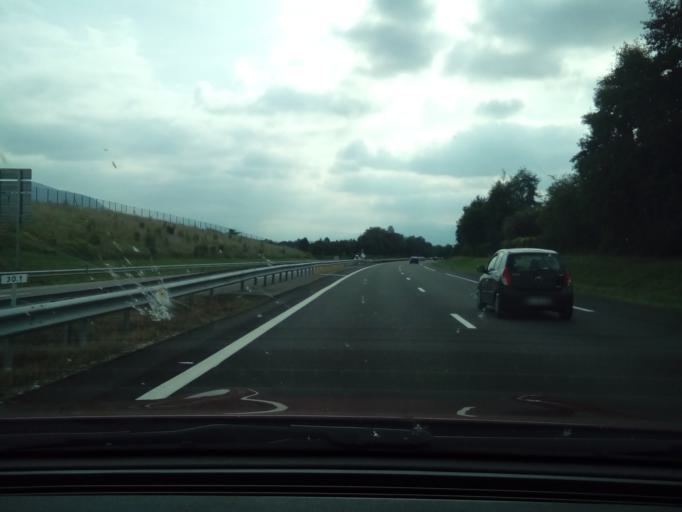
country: FR
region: Rhone-Alpes
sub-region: Departement de l'Isere
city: Saint-Sauveur
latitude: 45.1544
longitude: 5.3579
